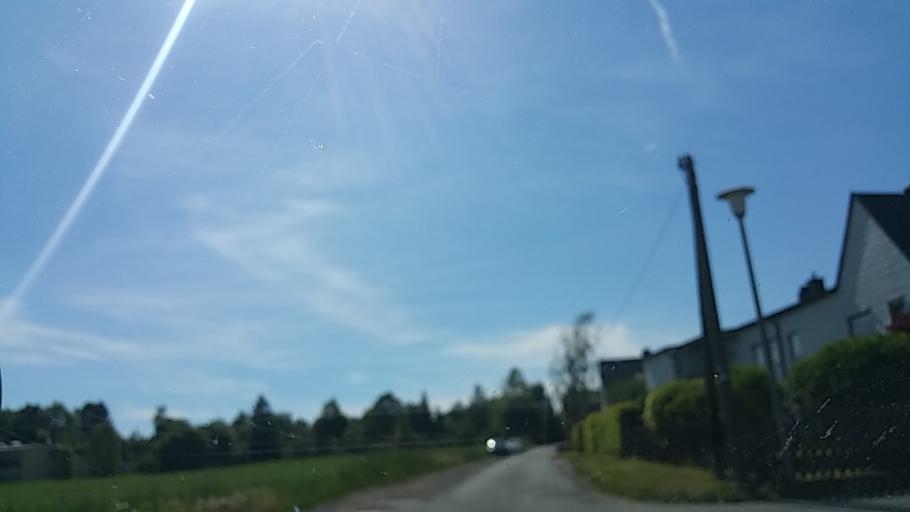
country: DE
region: Bavaria
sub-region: Upper Franconia
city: Schwarzenbach an der Saale
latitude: 50.2142
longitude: 11.9492
